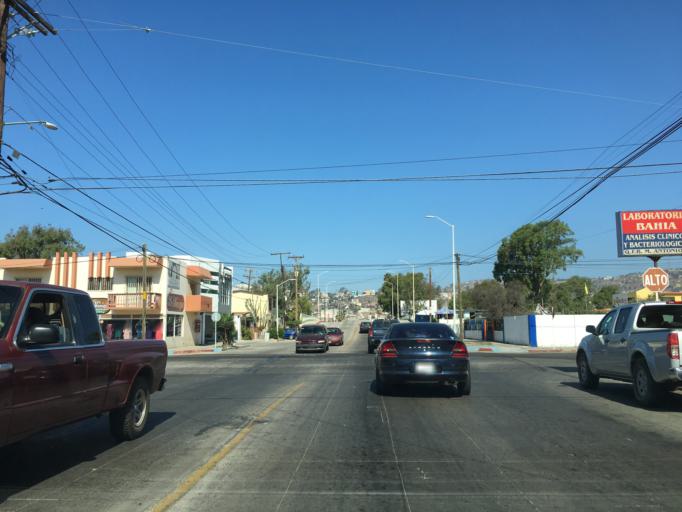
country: MX
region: Baja California
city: Ensenada
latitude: 31.8629
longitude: -116.6163
